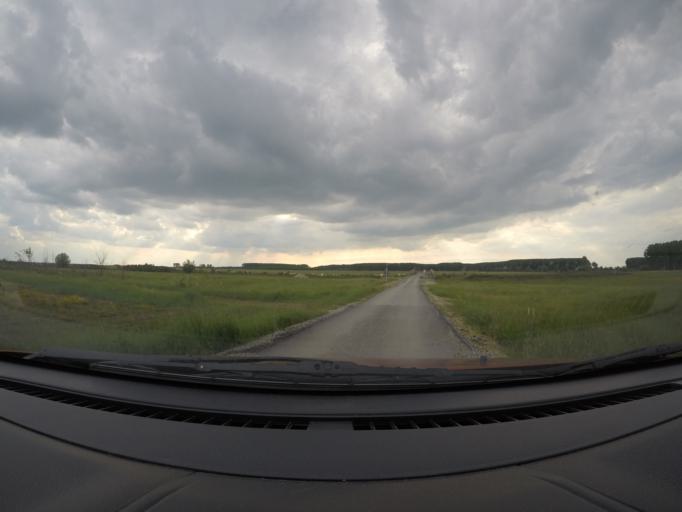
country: RS
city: Uzdin
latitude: 45.2029
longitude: 20.5945
